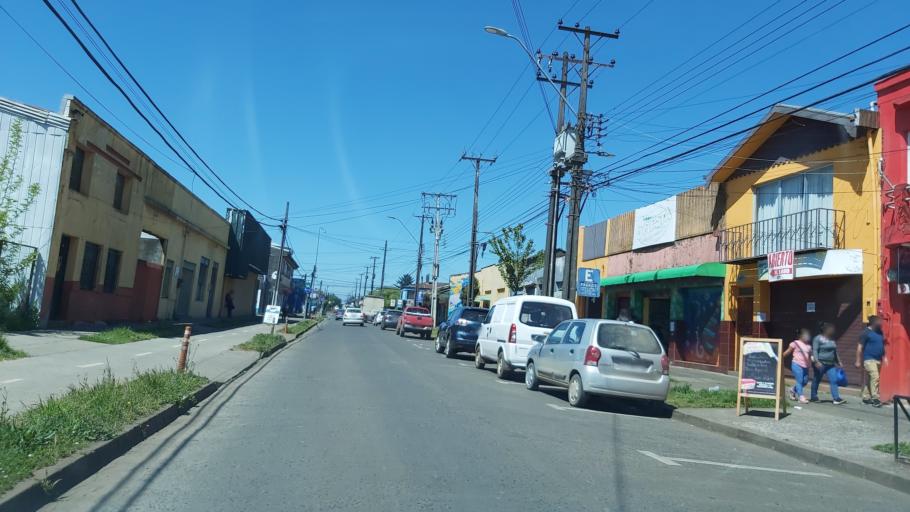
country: CL
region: Araucania
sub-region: Provincia de Malleco
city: Victoria
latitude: -38.2336
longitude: -72.3294
